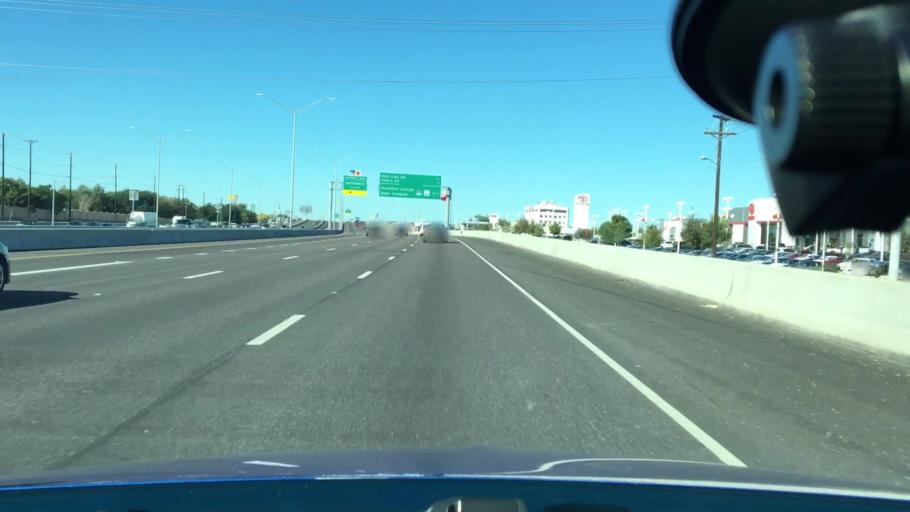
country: US
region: Texas
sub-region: Dallas County
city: Irving
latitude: 32.8373
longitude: -96.9679
